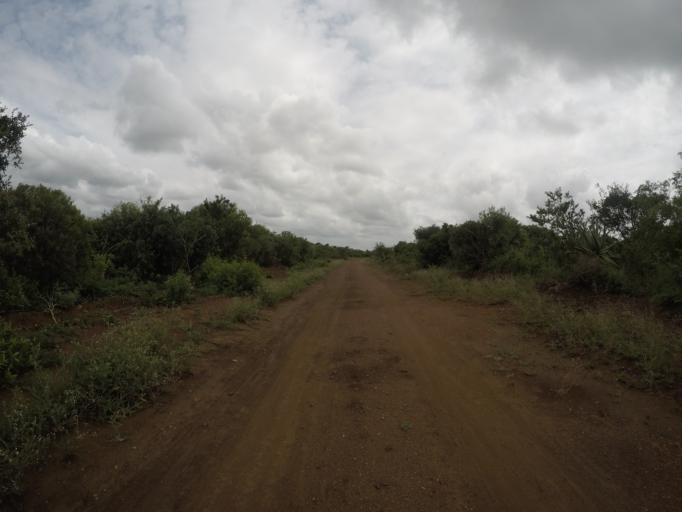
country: ZA
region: KwaZulu-Natal
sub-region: uThungulu District Municipality
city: Empangeni
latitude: -28.5866
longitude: 31.8696
